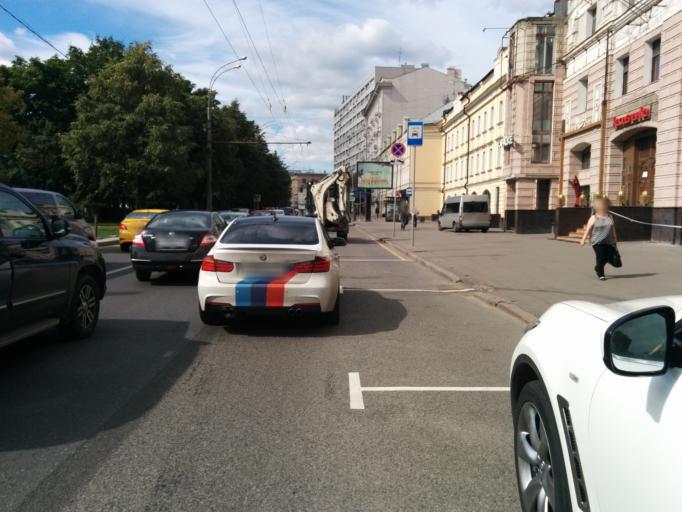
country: RU
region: Moscow
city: Moscow
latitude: 55.7721
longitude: 37.6008
